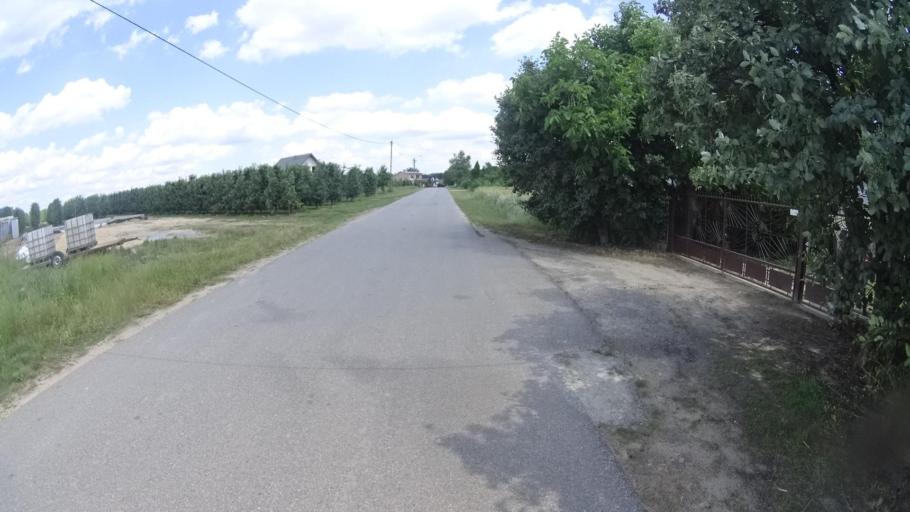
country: PL
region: Masovian Voivodeship
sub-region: Powiat grojecki
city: Goszczyn
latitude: 51.6945
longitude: 20.8680
